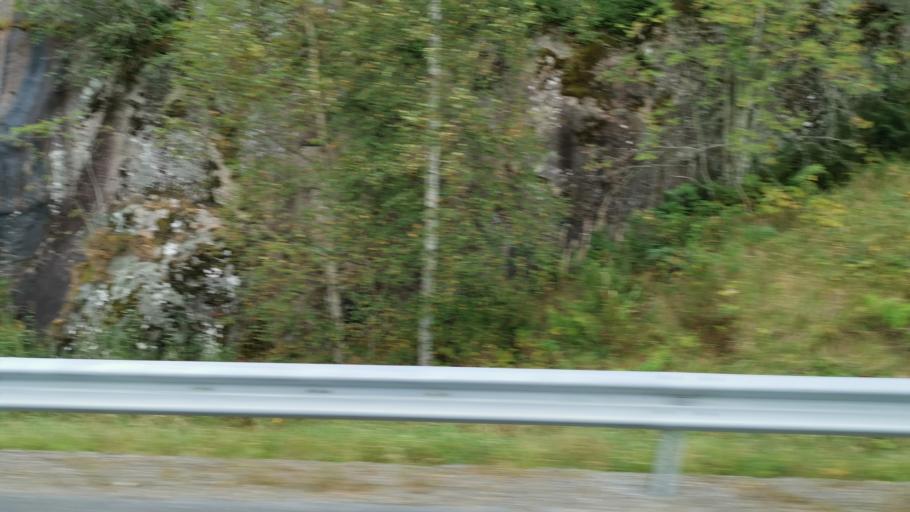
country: SE
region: Vaestra Goetaland
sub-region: Tanums Kommun
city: Tanumshede
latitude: 58.6449
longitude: 11.3385
